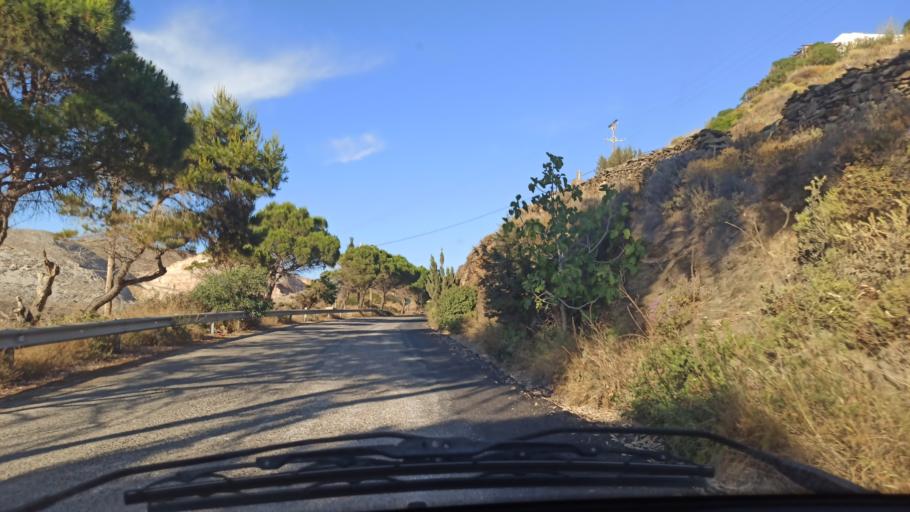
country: GR
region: South Aegean
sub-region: Nomos Kykladon
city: Ano Syros
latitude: 37.4427
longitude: 24.9073
